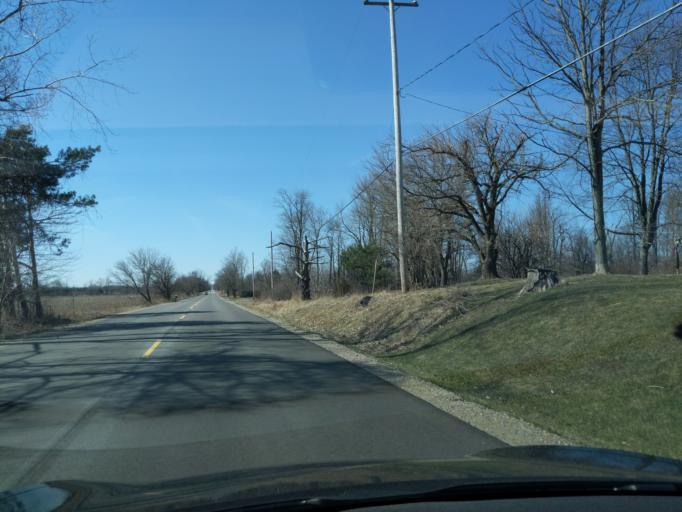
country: US
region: Michigan
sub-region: Eaton County
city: Grand Ledge
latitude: 42.7265
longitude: -84.7926
